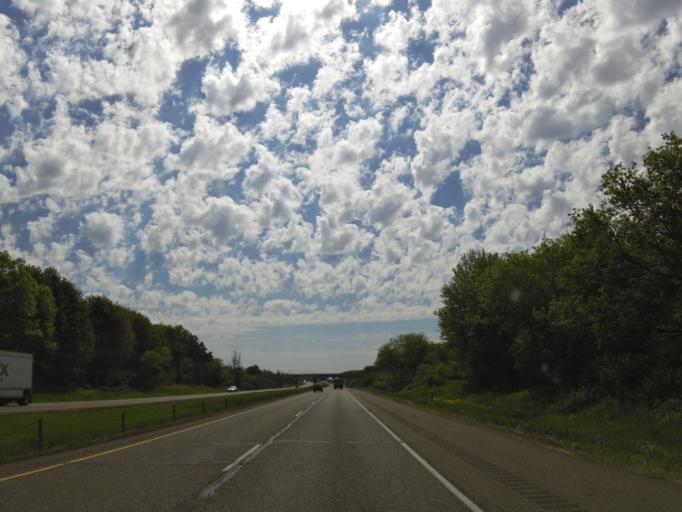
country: US
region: Wisconsin
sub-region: Dunn County
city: Colfax
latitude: 44.8690
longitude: -91.6943
